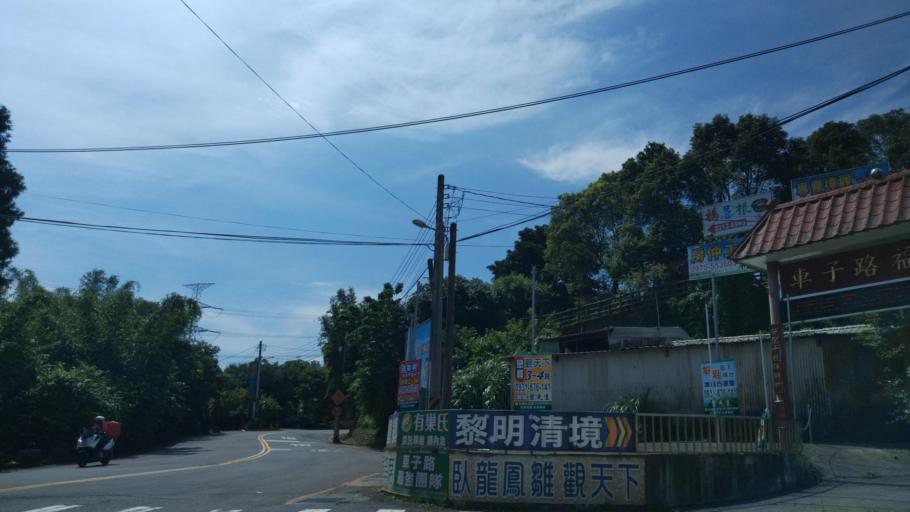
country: TW
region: Taipei
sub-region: Taipei
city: Banqiao
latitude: 24.9538
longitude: 121.5048
